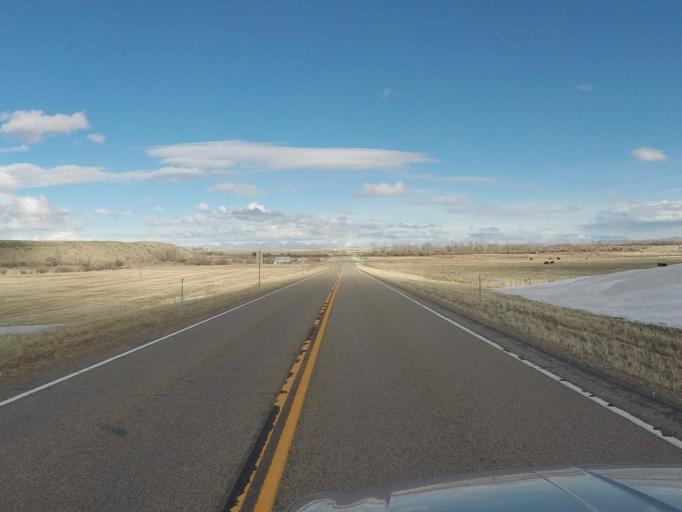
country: US
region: Montana
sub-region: Wheatland County
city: Harlowton
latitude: 46.4875
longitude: -110.3110
